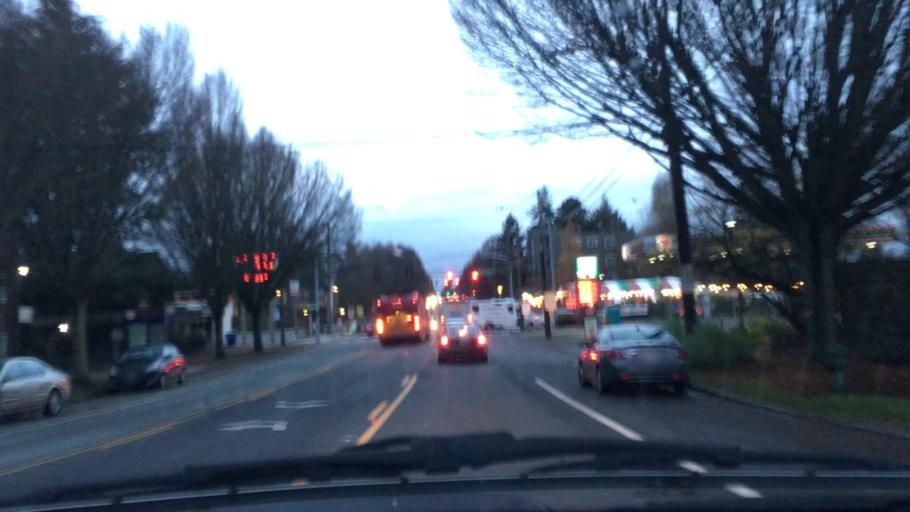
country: US
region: Washington
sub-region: King County
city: White Center
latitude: 47.5203
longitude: -122.3768
